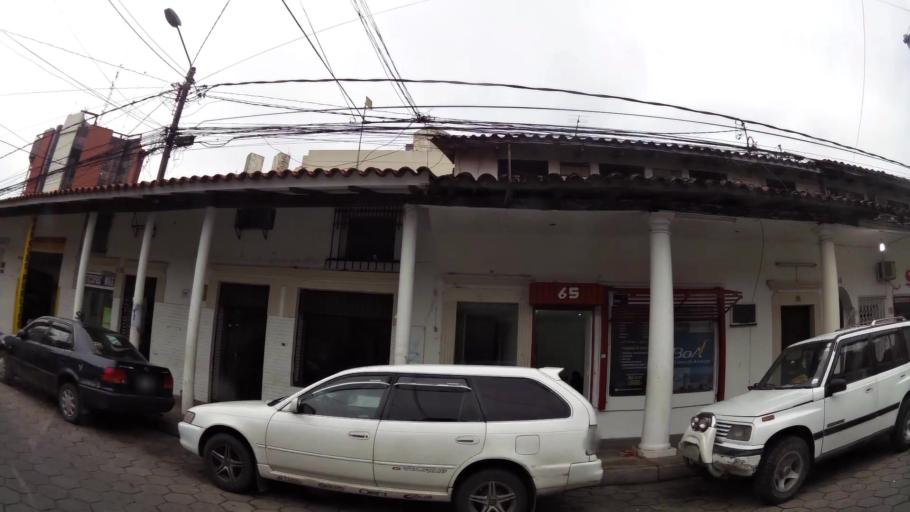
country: BO
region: Santa Cruz
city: Santa Cruz de la Sierra
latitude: -17.7861
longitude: -63.1819
